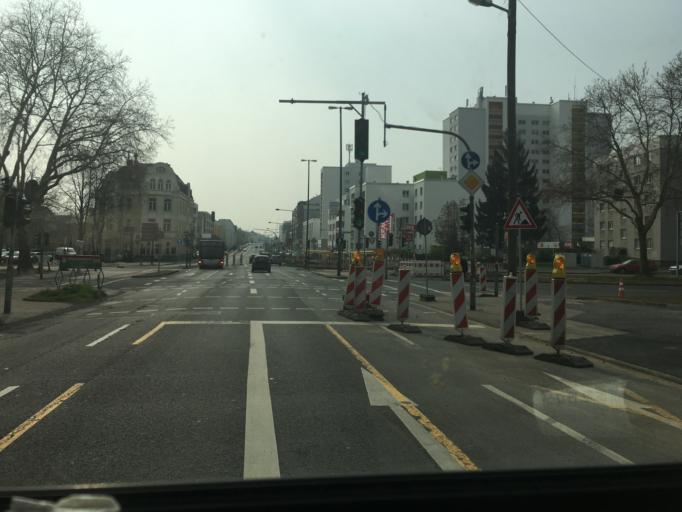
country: DE
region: North Rhine-Westphalia
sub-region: Regierungsbezirk Koln
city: Bayenthal
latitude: 50.9043
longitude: 6.9644
